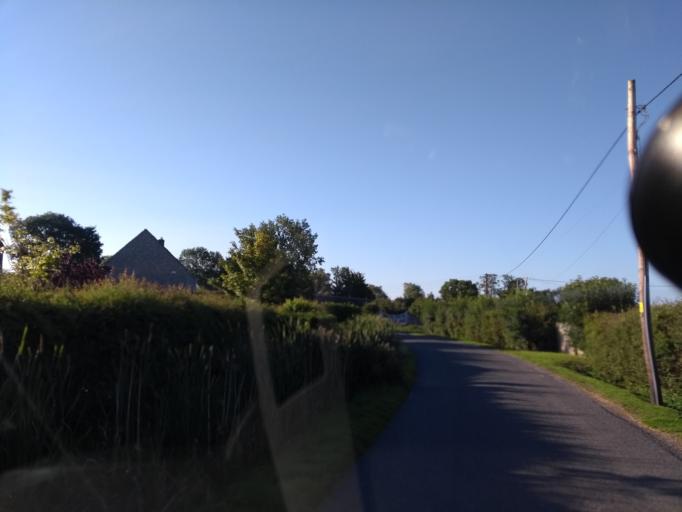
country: GB
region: England
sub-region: Somerset
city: Axbridge
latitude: 51.2679
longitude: -2.8709
